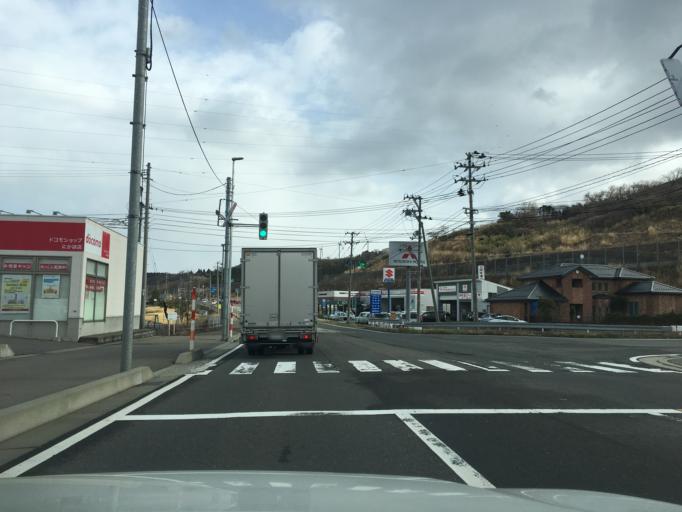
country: JP
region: Yamagata
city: Yuza
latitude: 39.2902
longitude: 139.9732
